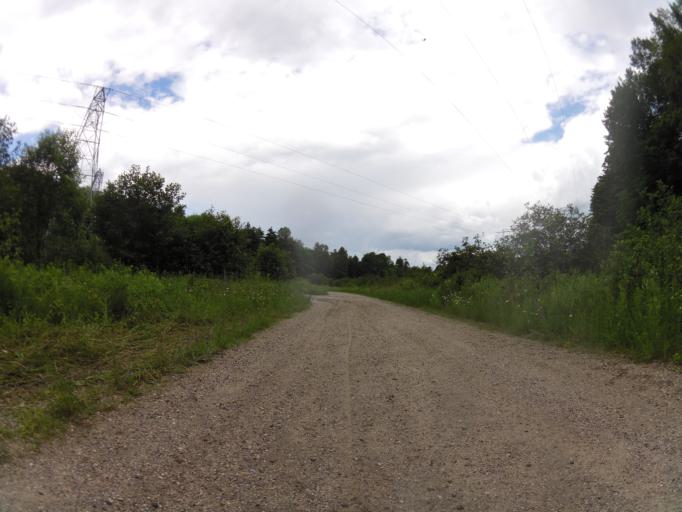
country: CA
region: Ontario
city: Renfrew
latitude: 45.0739
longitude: -76.7226
